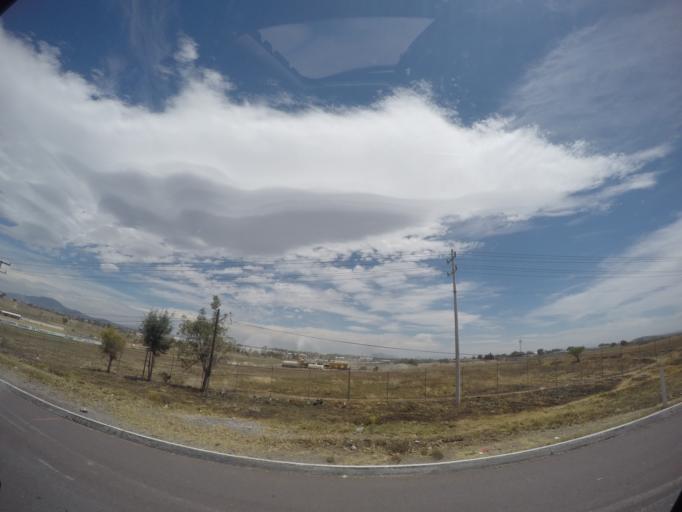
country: MX
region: Mexico
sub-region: Cuautitlan
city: Barrio Tlatenco
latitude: 19.7373
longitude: -99.2111
